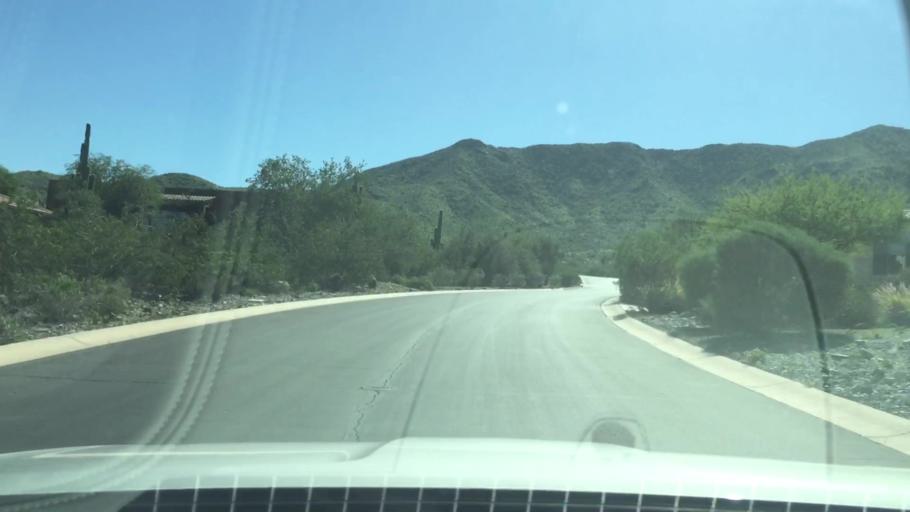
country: US
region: Arizona
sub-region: Maricopa County
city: Laveen
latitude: 33.3546
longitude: -112.0984
